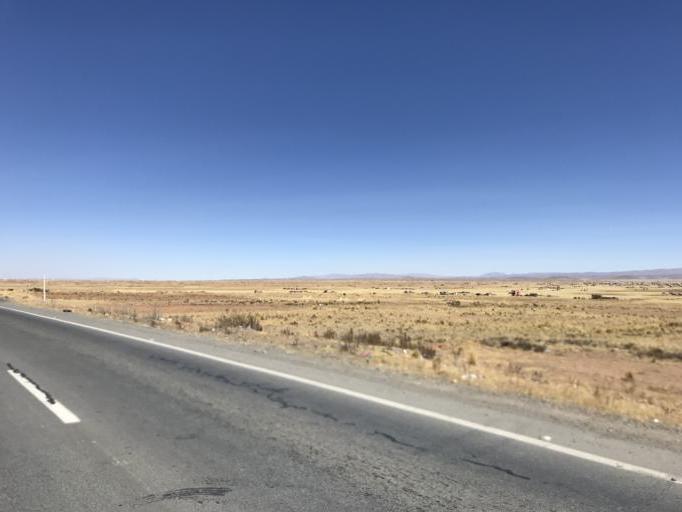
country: BO
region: La Paz
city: Batallas
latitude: -16.4030
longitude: -68.3569
